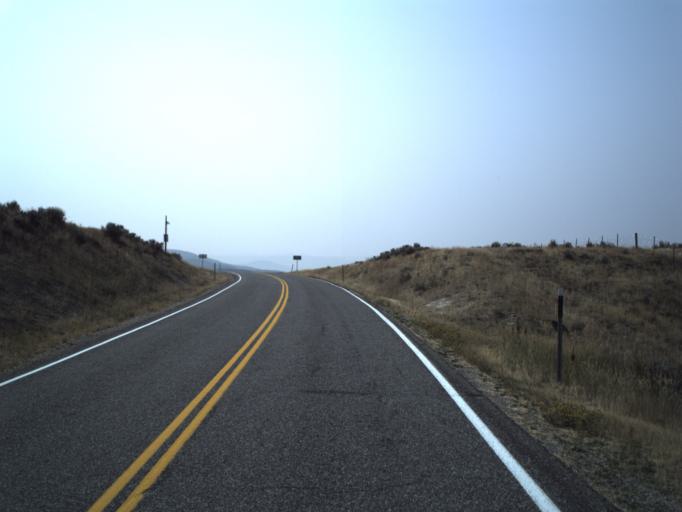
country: US
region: Utah
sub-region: Morgan County
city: Morgan
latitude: 40.9555
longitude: -111.5494
